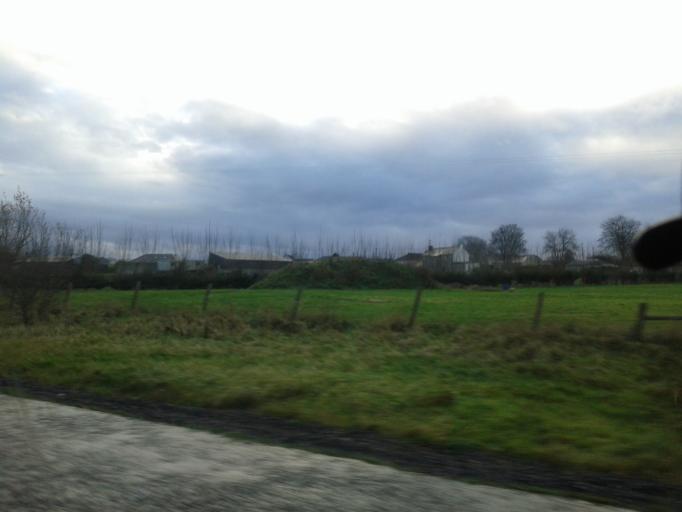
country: IE
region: Leinster
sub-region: Lu
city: Ardee
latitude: 53.8915
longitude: -6.5788
